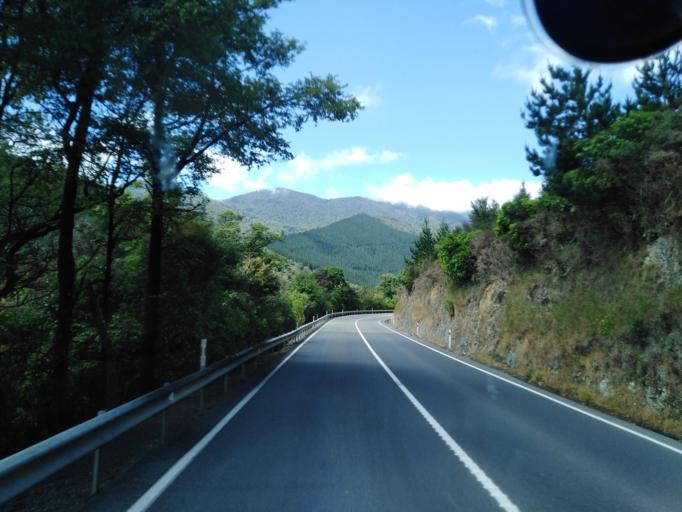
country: NZ
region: Nelson
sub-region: Nelson City
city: Nelson
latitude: -41.2251
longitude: 173.4361
